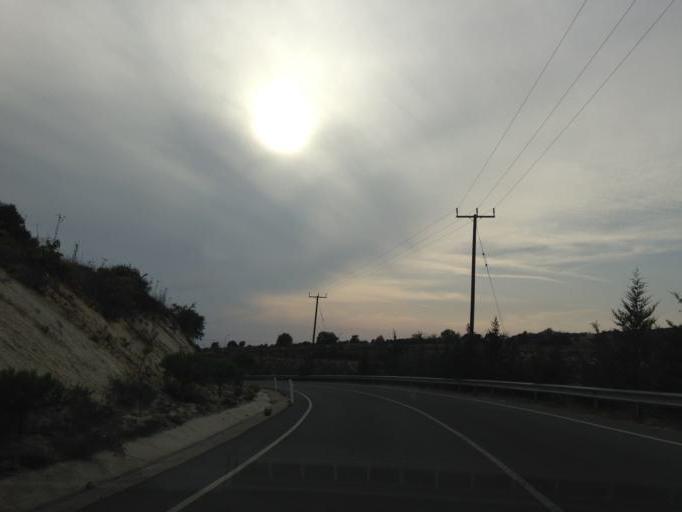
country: CY
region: Limassol
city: Pachna
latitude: 34.7713
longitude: 32.7927
